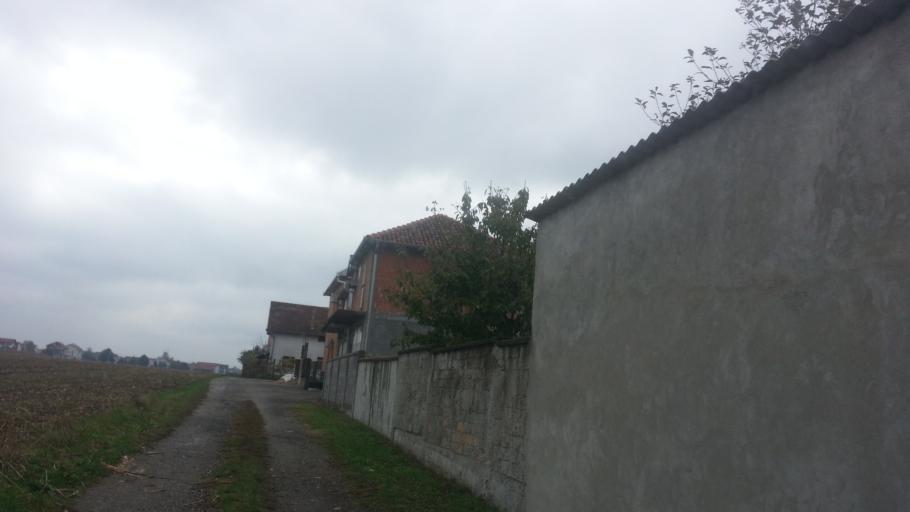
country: RS
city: Novi Banovci
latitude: 44.9186
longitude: 20.2825
